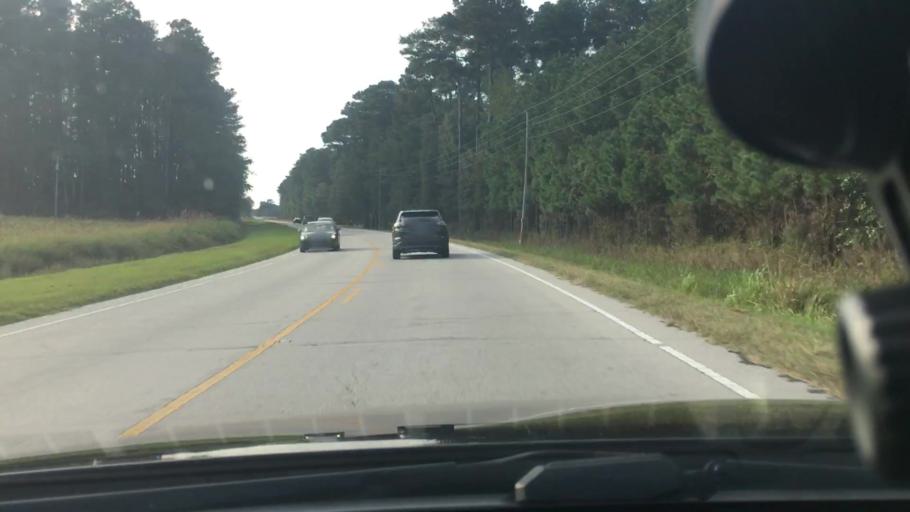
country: US
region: North Carolina
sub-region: Pitt County
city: Windsor
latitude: 35.4693
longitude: -77.2799
